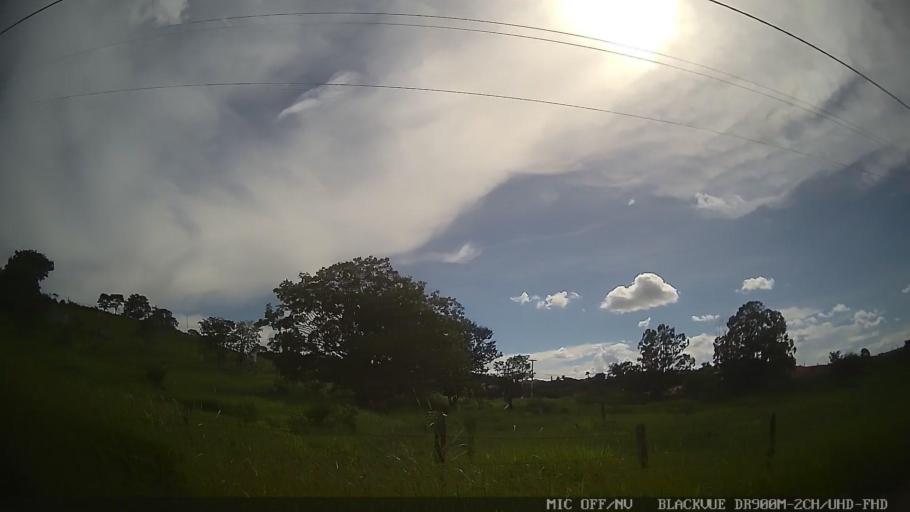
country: BR
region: Sao Paulo
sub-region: Conchas
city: Conchas
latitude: -23.0190
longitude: -47.9990
